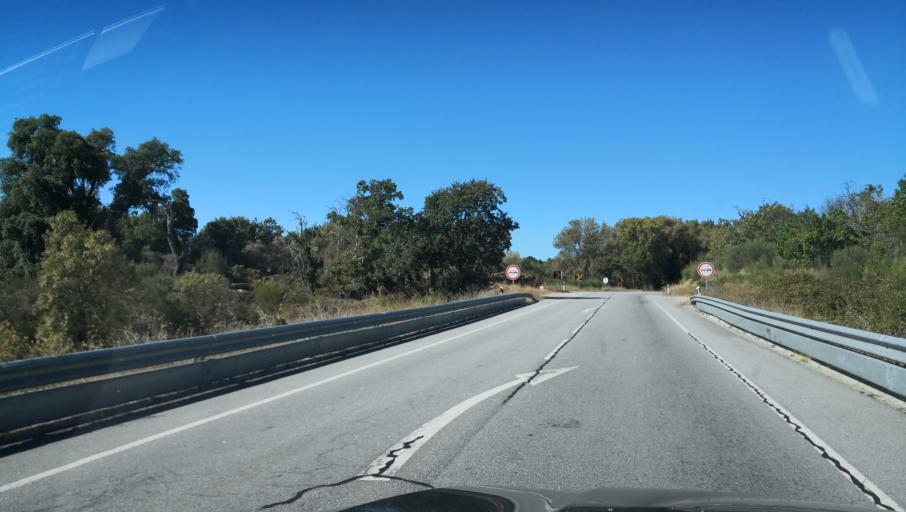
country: PT
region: Vila Real
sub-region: Valpacos
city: Valpacos
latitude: 41.6442
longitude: -7.3192
